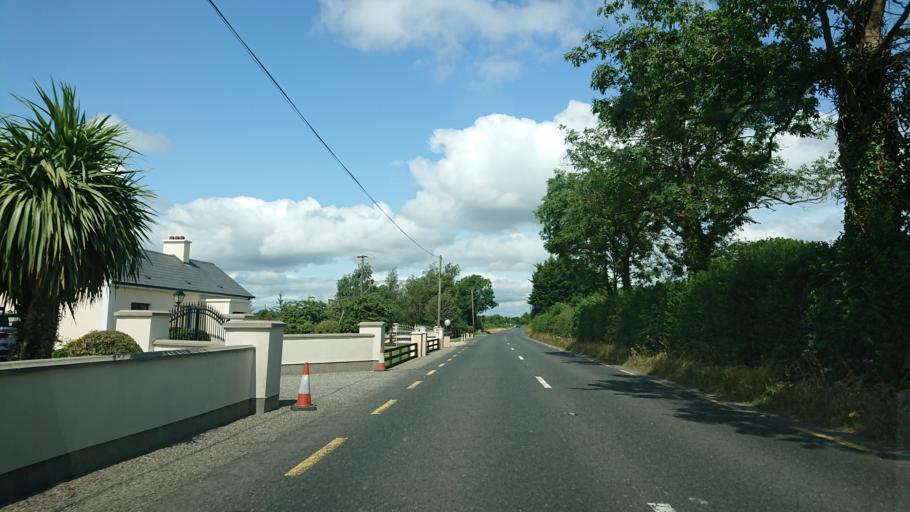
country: IE
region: Leinster
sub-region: Kildare
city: Kilcock
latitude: 53.3617
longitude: -6.6973
